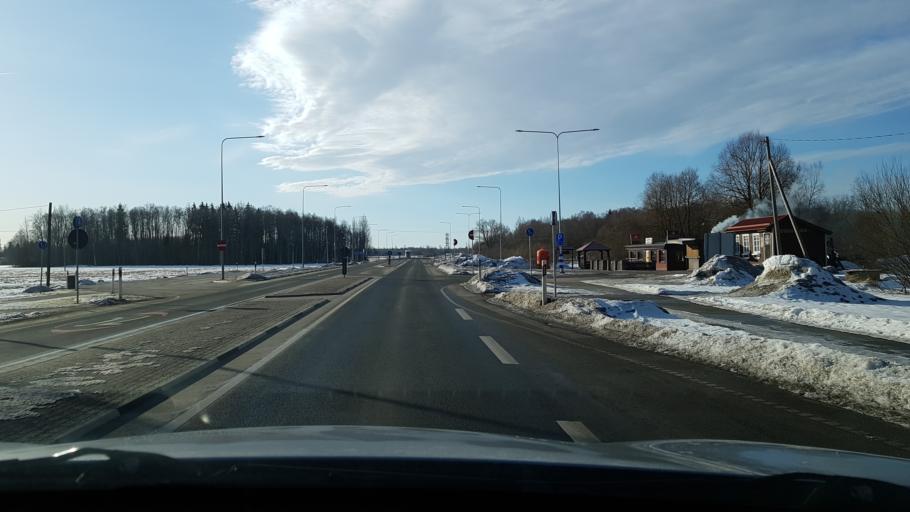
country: EE
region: Viljandimaa
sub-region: Vohma linn
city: Vohma
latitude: 58.6296
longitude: 25.5710
